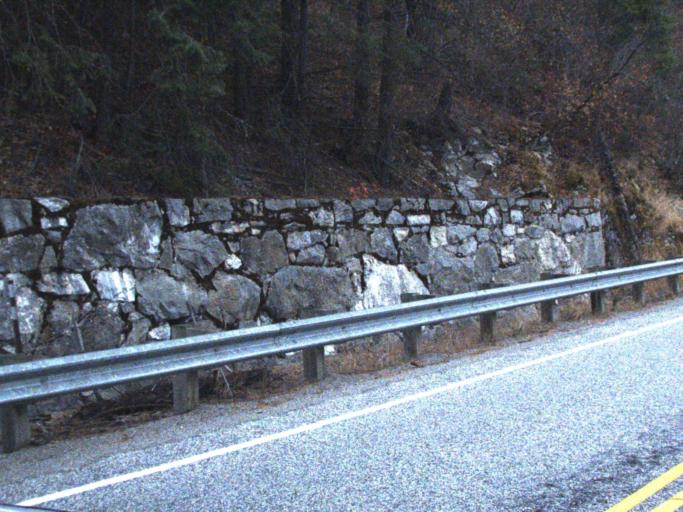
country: US
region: Washington
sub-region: Stevens County
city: Kettle Falls
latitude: 48.7907
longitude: -118.1582
